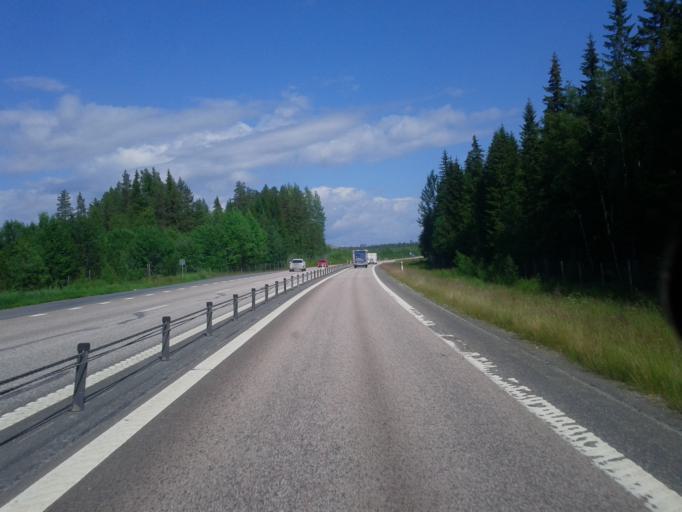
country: SE
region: Vaesternorrland
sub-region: OErnskoeldsviks Kommun
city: Husum
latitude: 63.4387
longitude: 19.2122
